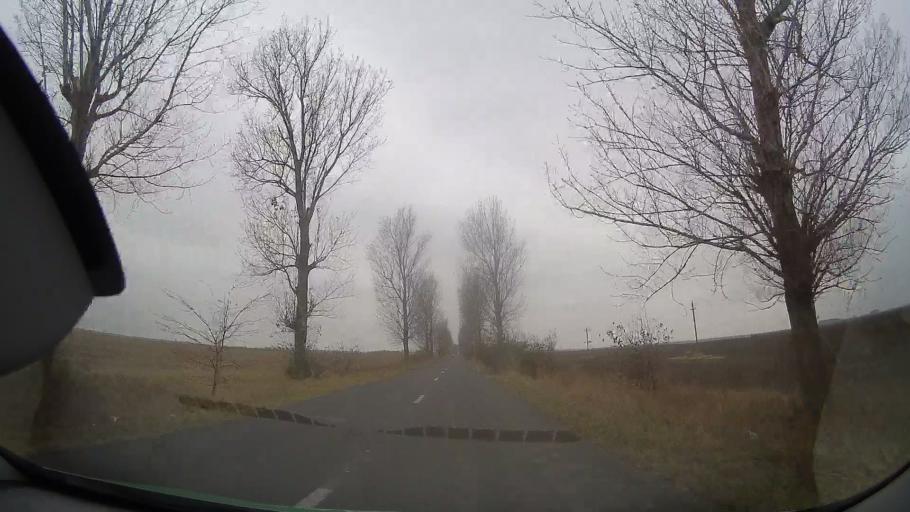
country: RO
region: Buzau
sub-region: Comuna Scutelnici
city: Scutelnici
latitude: 44.8394
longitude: 26.8677
